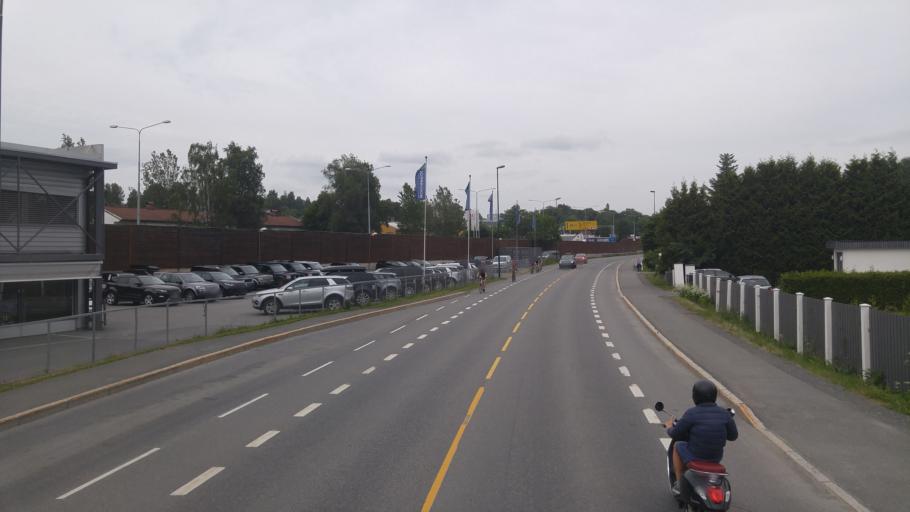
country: NO
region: Akershus
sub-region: Baerum
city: Sandvika
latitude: 59.8957
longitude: 10.5614
